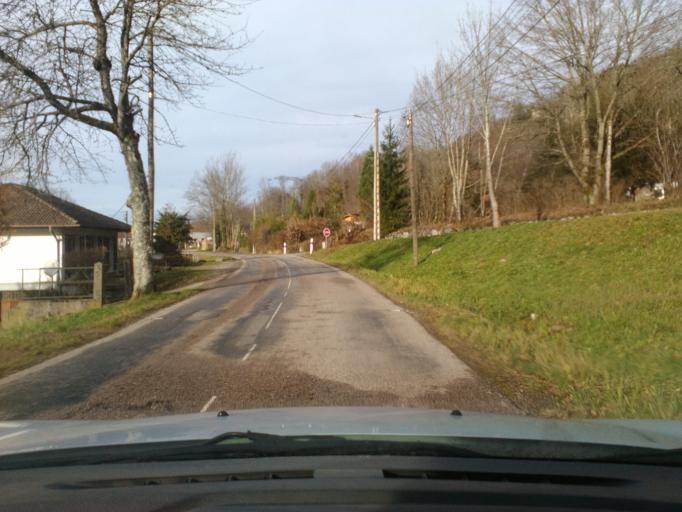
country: FR
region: Lorraine
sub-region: Departement des Vosges
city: Fraize
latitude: 48.1625
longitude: 6.9848
